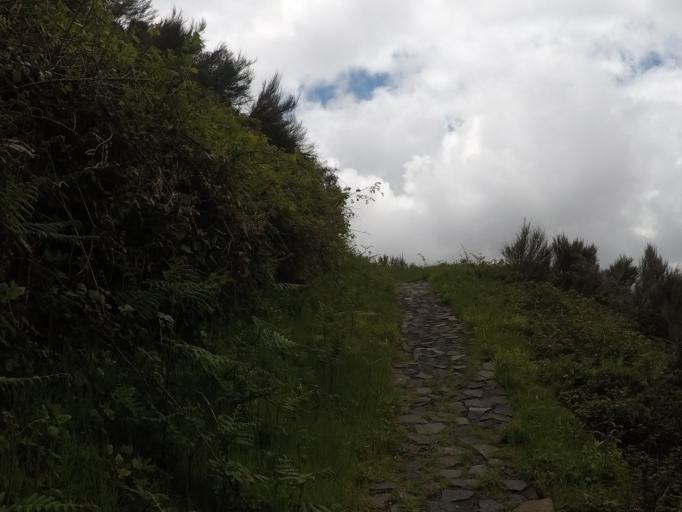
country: PT
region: Madeira
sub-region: Camara de Lobos
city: Curral das Freiras
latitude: 32.7388
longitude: -17.0015
